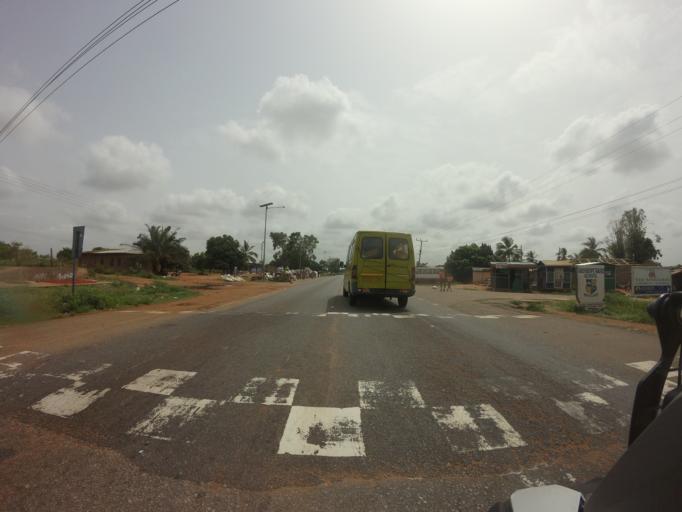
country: GH
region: Volta
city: Anloga
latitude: 5.8930
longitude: 0.4940
